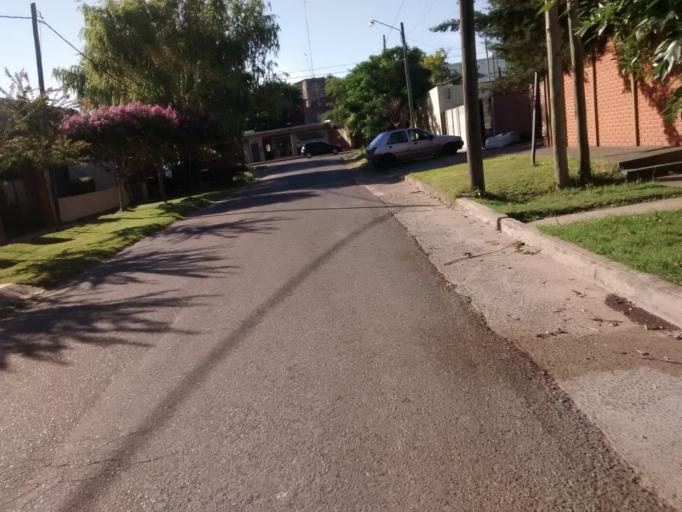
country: AR
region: Buenos Aires
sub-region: Partido de La Plata
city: La Plata
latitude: -34.8553
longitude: -58.0802
